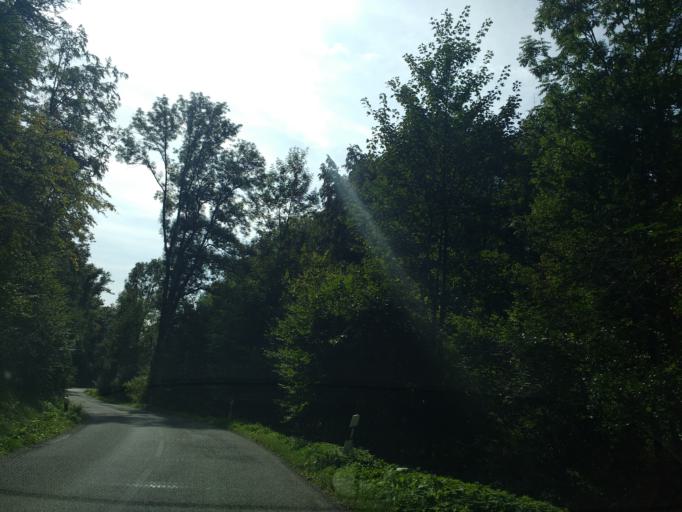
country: DE
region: Hesse
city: Witzenhausen
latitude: 51.3999
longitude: 9.8304
